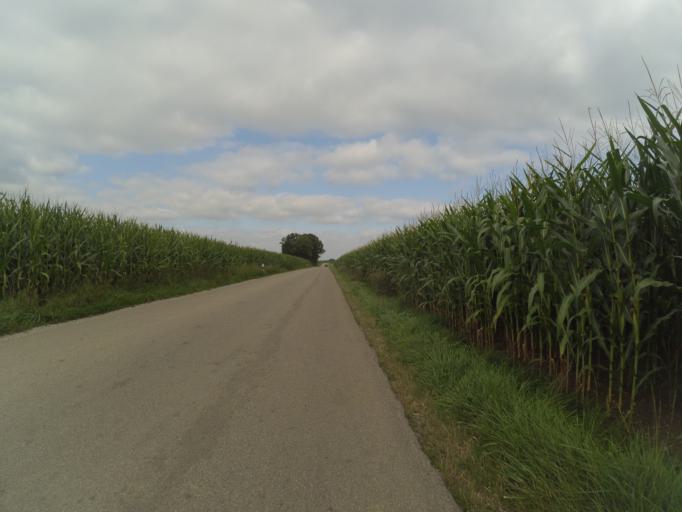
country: DE
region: Bavaria
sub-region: Swabia
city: Buchloe
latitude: 48.0502
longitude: 10.7395
